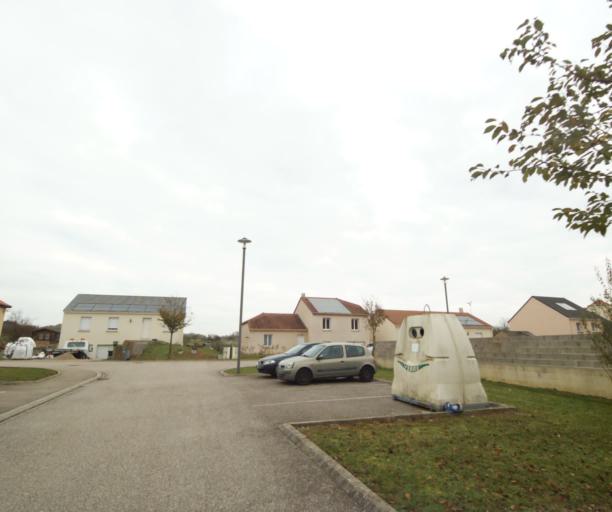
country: FR
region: Lorraine
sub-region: Departement de Meurthe-et-Moselle
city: Mancieulles
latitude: 49.2756
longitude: 5.9069
